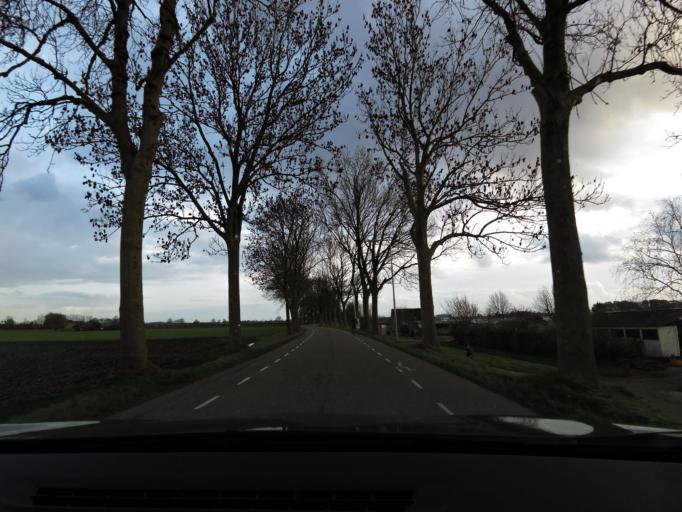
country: NL
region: South Holland
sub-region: Gemeente Binnenmaas
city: Heinenoord
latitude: 51.8238
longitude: 4.4883
